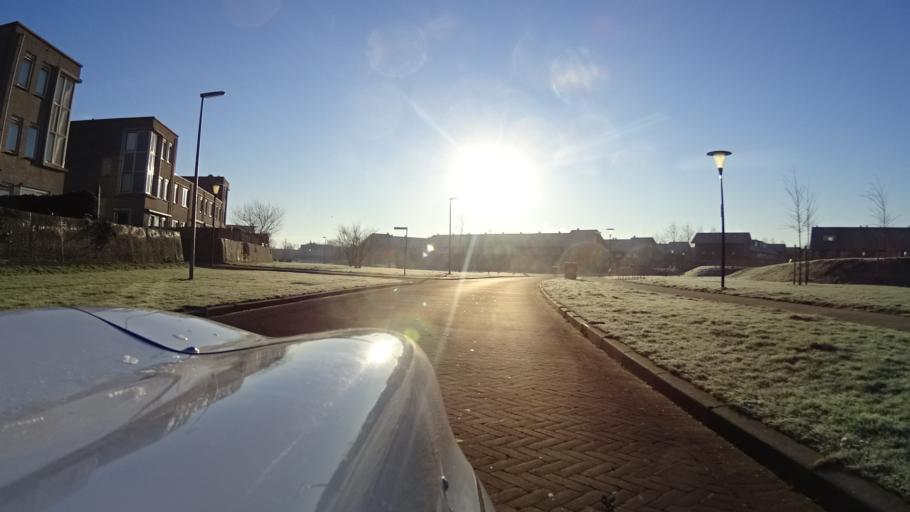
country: NL
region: South Holland
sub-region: Gemeente Barendrecht
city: Barendrecht
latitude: 51.8622
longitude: 4.5067
